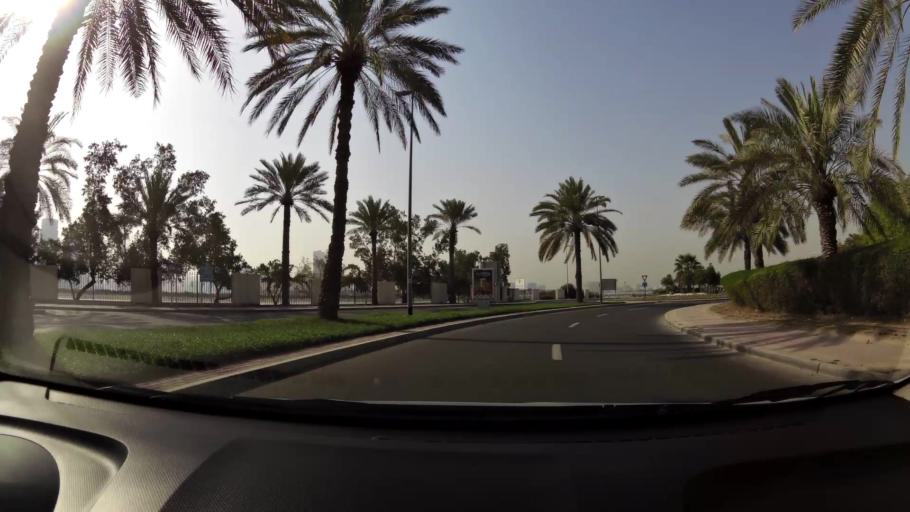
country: AE
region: Ash Shariqah
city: Sharjah
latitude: 25.3157
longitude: 55.3483
